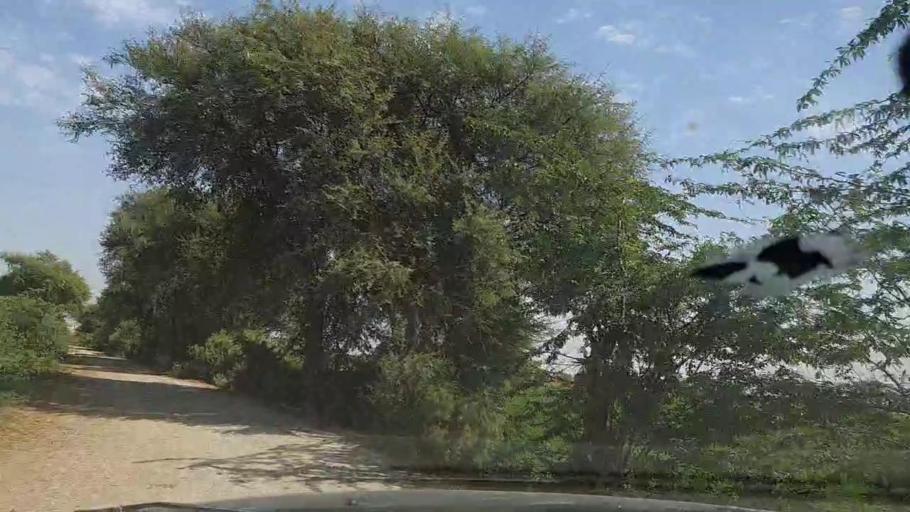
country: PK
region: Sindh
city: Daro Mehar
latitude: 24.6619
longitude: 68.0839
